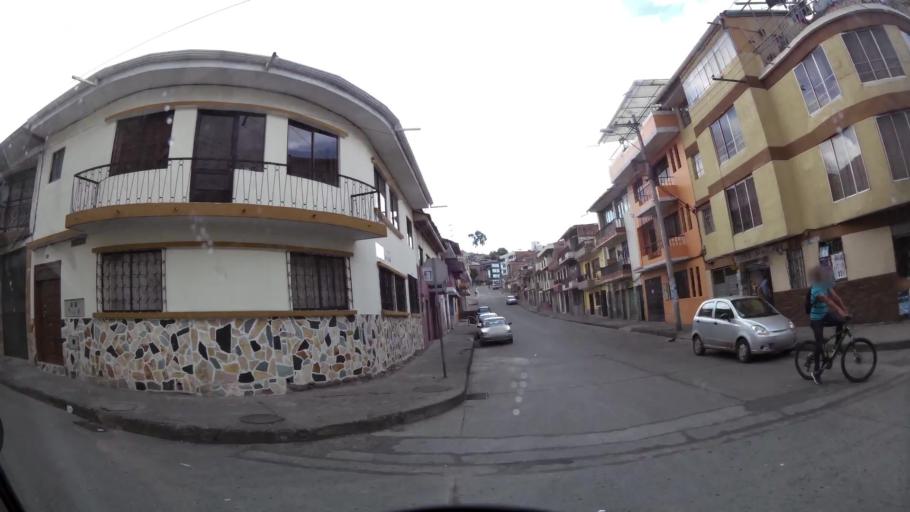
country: EC
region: Azuay
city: Cuenca
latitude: -2.8908
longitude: -79.0120
